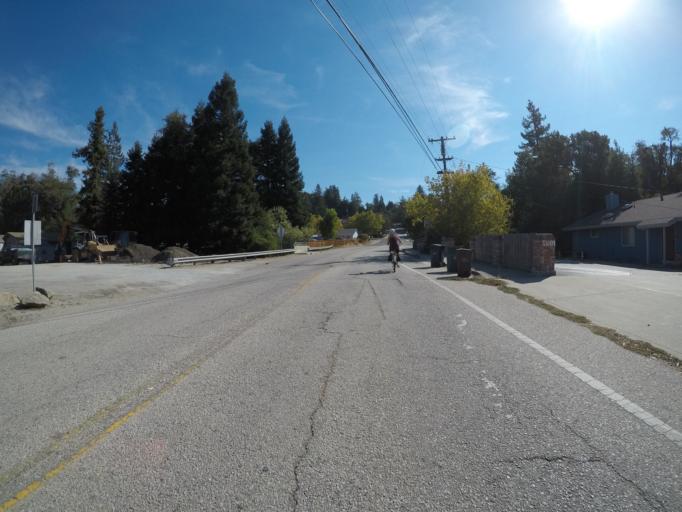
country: US
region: California
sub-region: Santa Cruz County
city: Scotts Valley
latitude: 37.0606
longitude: -122.0024
